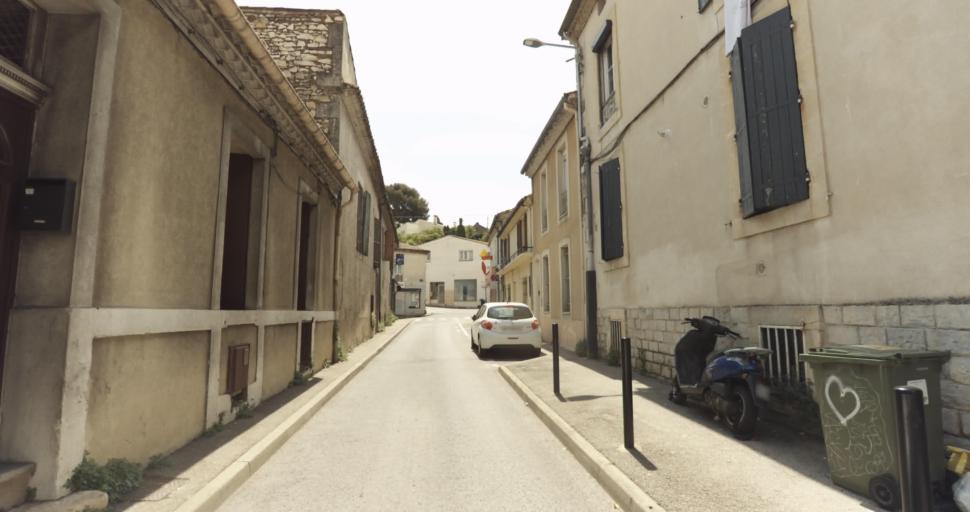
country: FR
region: Languedoc-Roussillon
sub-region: Departement du Gard
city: Nimes
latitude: 43.8470
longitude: 4.3628
